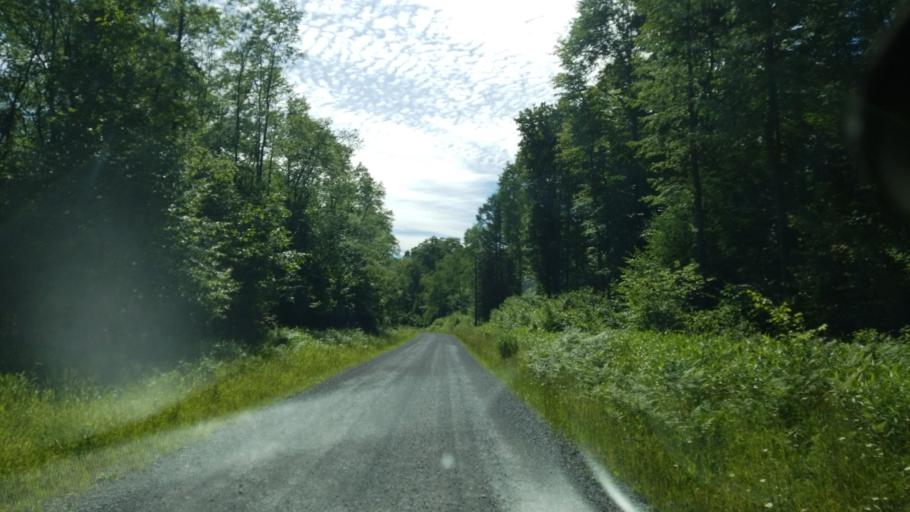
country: US
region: Pennsylvania
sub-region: Clearfield County
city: Clearfield
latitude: 41.1920
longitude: -78.4738
